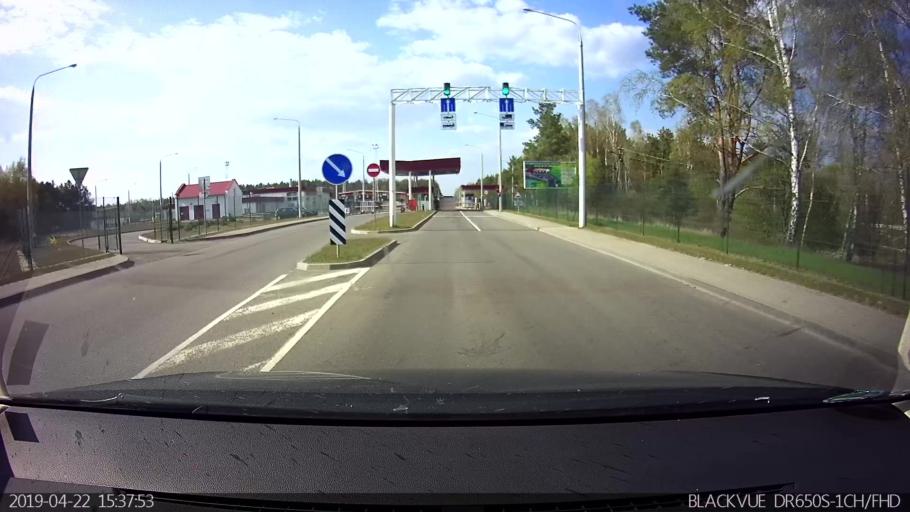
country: PL
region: Podlasie
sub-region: Powiat hajnowski
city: Czeremcha
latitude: 52.4645
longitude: 23.3616
